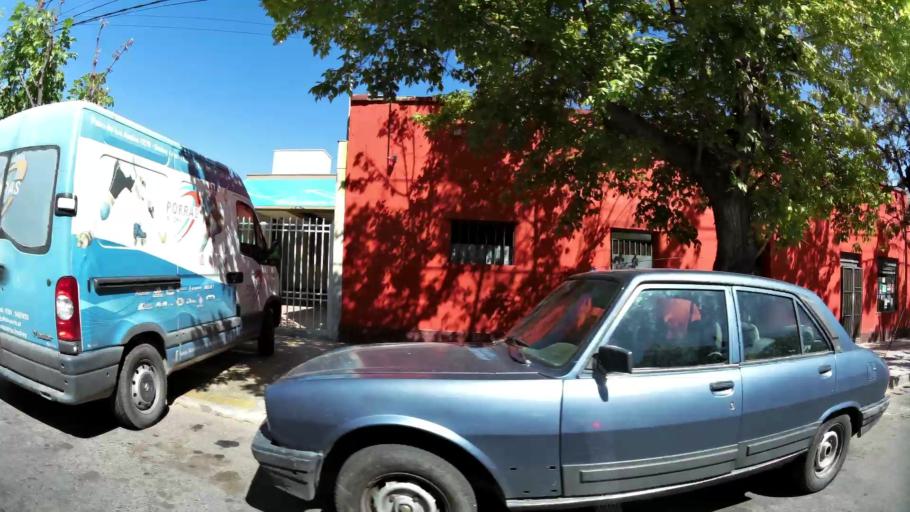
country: AR
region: Mendoza
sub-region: Departamento de Godoy Cruz
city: Godoy Cruz
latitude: -32.9129
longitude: -68.8599
